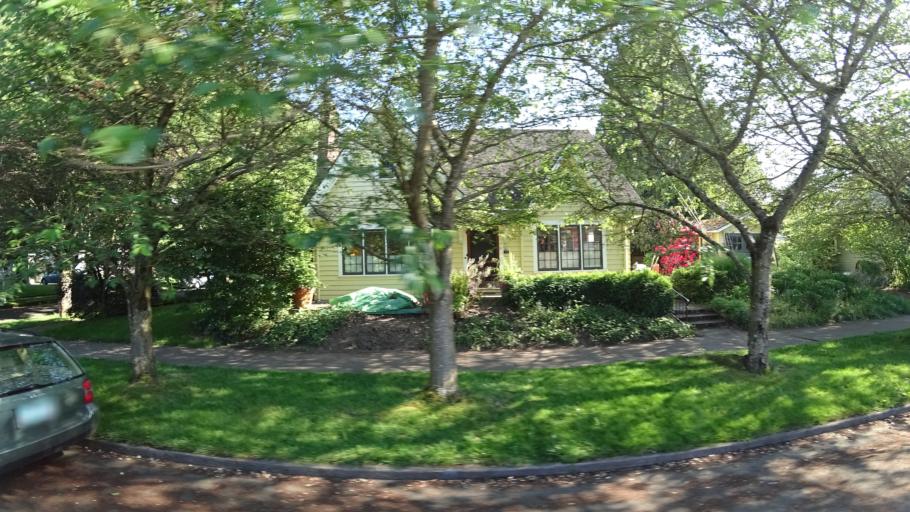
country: US
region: Oregon
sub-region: Multnomah County
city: Portland
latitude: 45.5467
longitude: -122.6404
